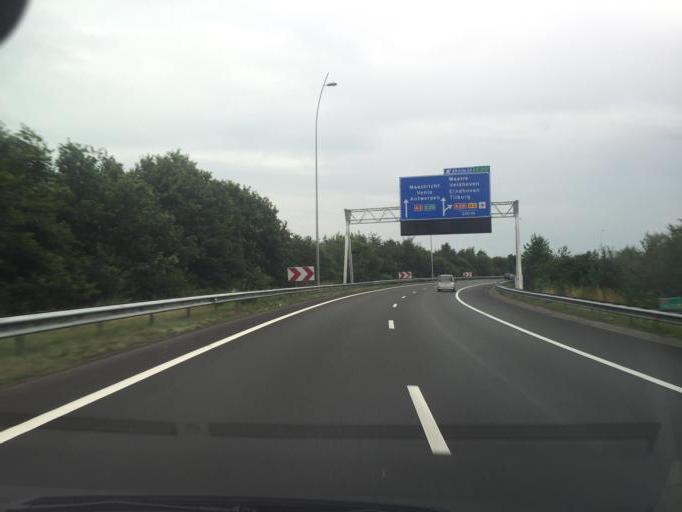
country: NL
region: North Brabant
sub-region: Gemeente Best
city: Best
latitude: 51.4922
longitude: 5.4288
